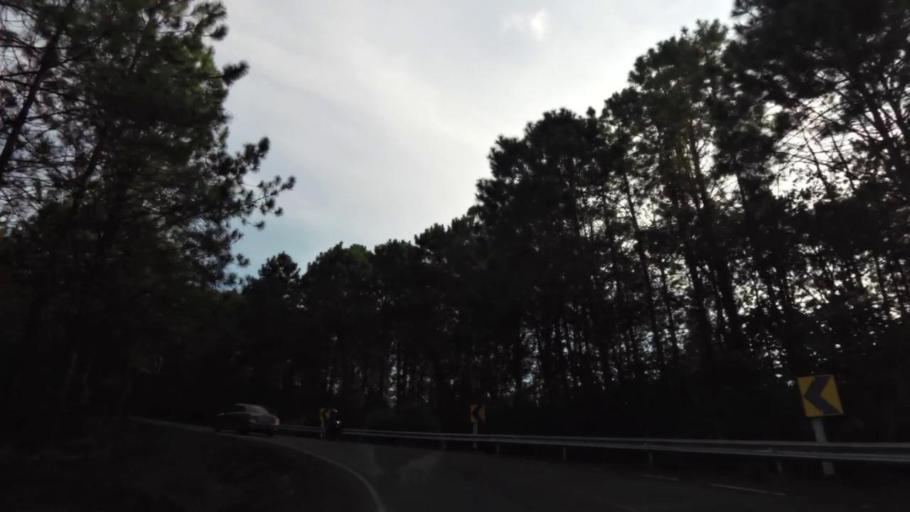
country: TH
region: Chiang Rai
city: Khun Tan
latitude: 19.8668
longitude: 100.3325
